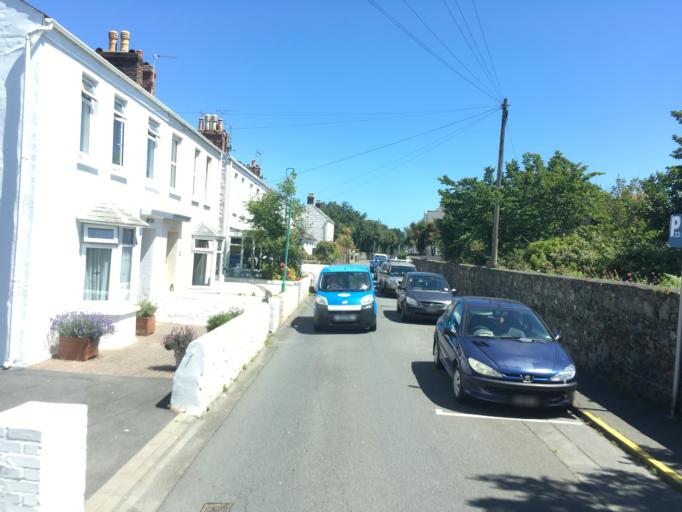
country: GG
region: St Peter Port
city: Saint Peter Port
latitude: 49.4803
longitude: -2.5194
